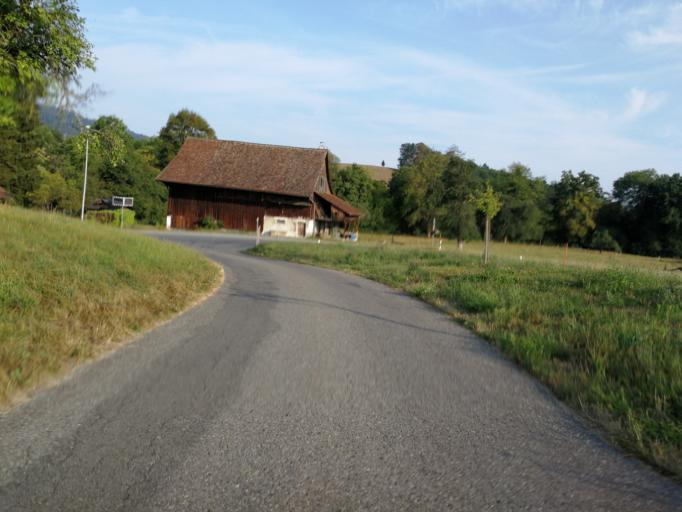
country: CH
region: Zurich
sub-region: Bezirk Uster
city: Esslingen
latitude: 47.2899
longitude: 8.7153
